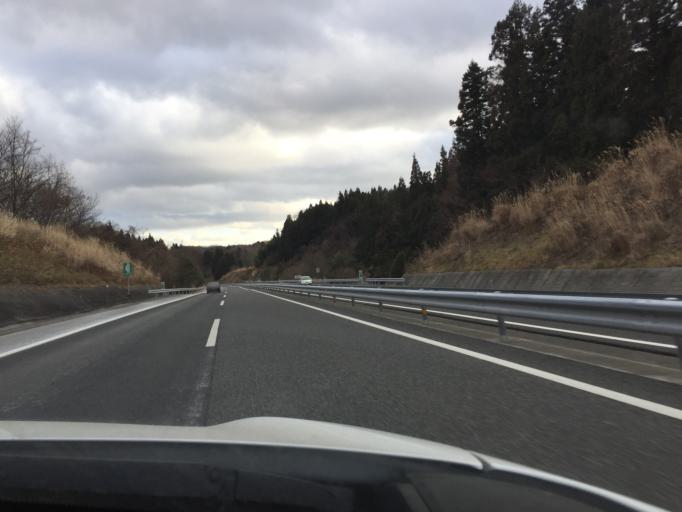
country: JP
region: Fukushima
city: Funehikimachi-funehiki
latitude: 37.2609
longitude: 140.6479
